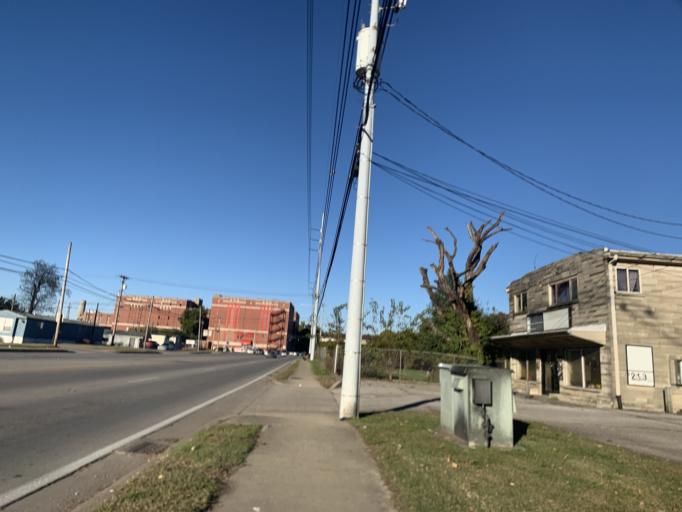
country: US
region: Kentucky
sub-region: Jefferson County
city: Shively
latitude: 38.2115
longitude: -85.7856
